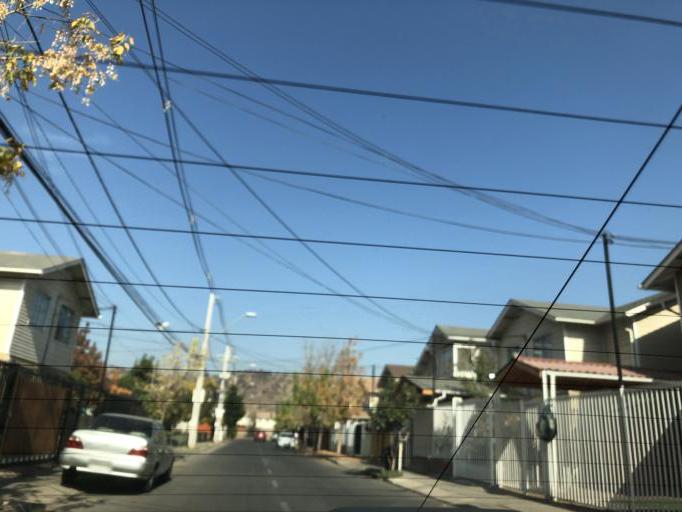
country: CL
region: Santiago Metropolitan
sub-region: Provincia de Cordillera
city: Puente Alto
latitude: -33.5967
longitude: -70.5496
